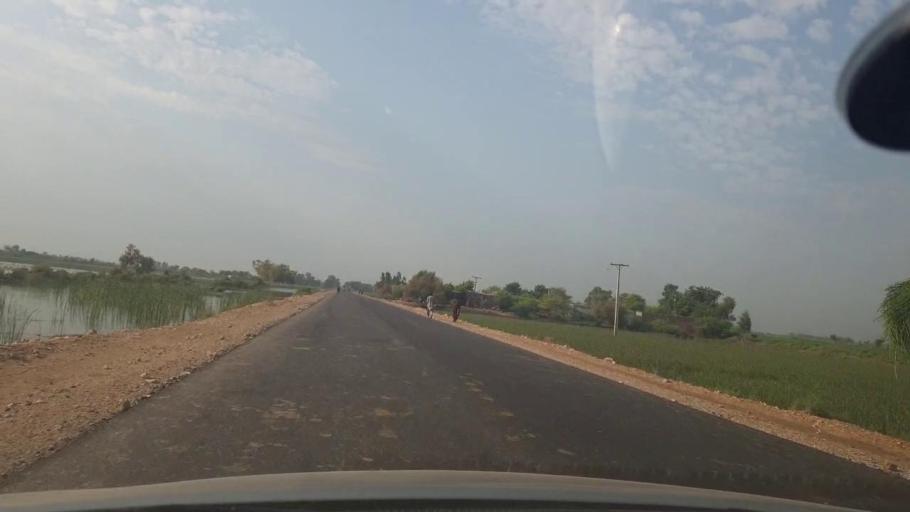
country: PK
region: Sindh
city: Jacobabad
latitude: 28.1188
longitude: 68.3274
